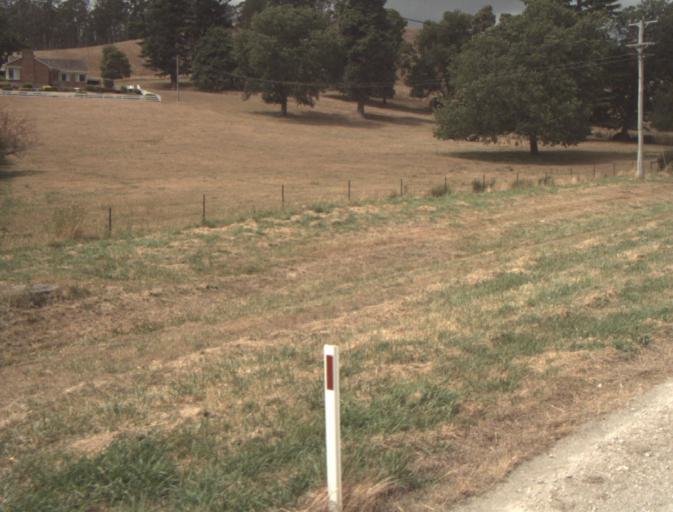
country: AU
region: Tasmania
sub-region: Launceston
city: Mayfield
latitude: -41.2579
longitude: 147.2176
